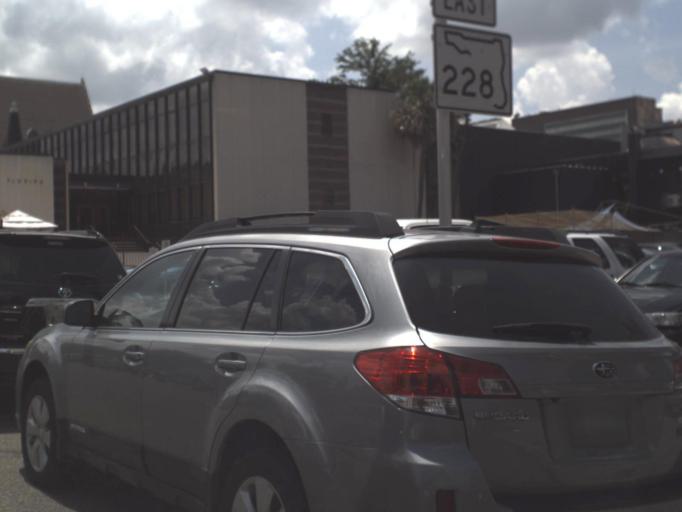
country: US
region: Florida
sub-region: Duval County
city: Jacksonville
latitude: 30.3284
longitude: -81.6570
